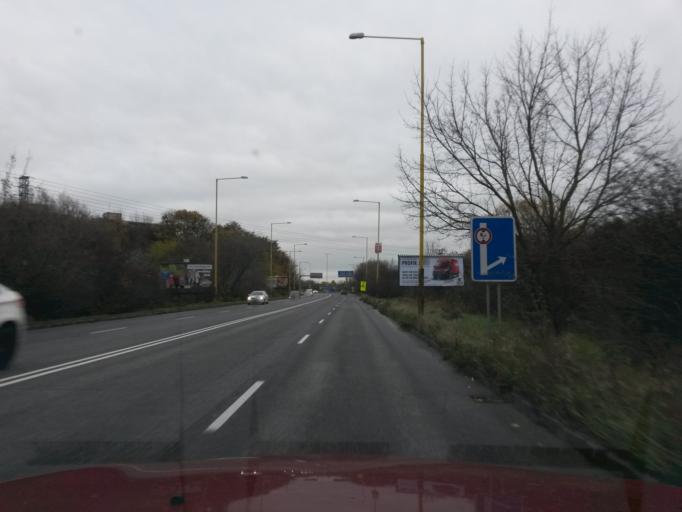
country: SK
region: Kosicky
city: Kosice
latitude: 48.6972
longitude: 21.2278
